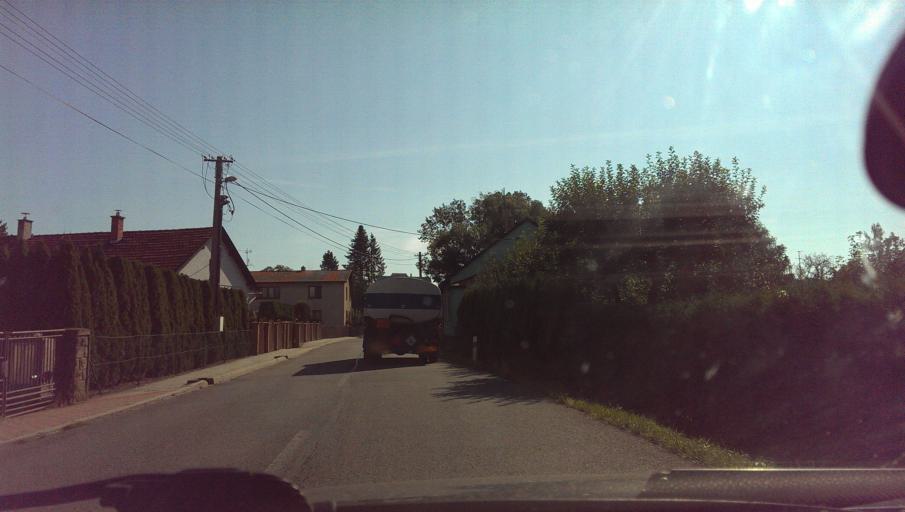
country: CZ
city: Staric
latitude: 49.6838
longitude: 18.2459
